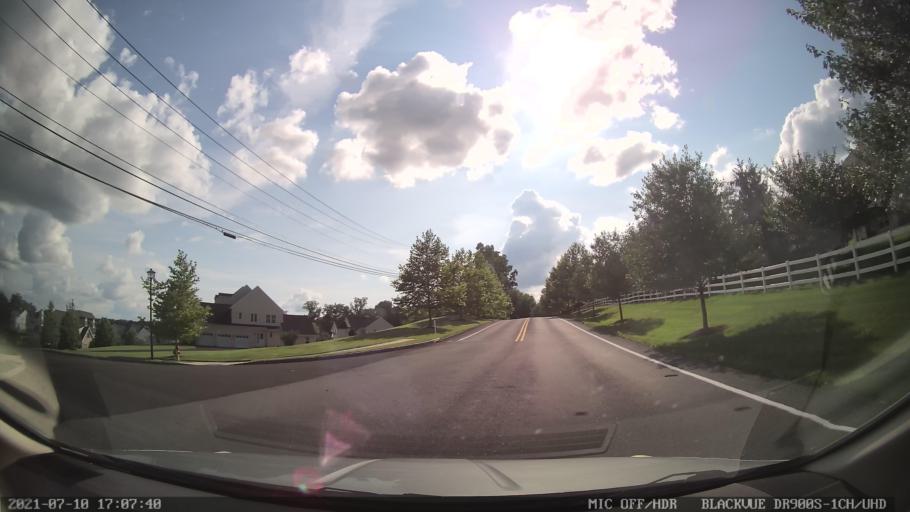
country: US
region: Pennsylvania
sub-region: Lehigh County
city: Coopersburg
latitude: 40.5255
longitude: -75.3987
